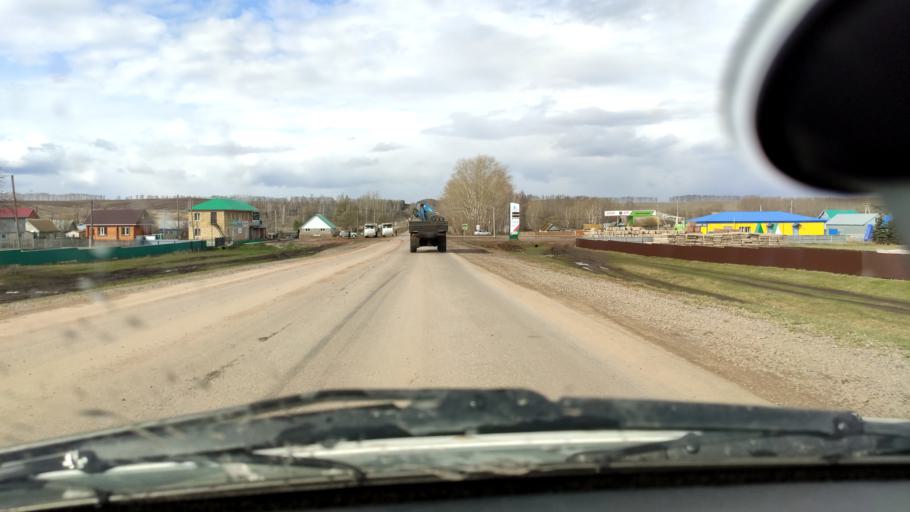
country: RU
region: Bashkortostan
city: Buzdyak
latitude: 54.6862
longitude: 54.5547
